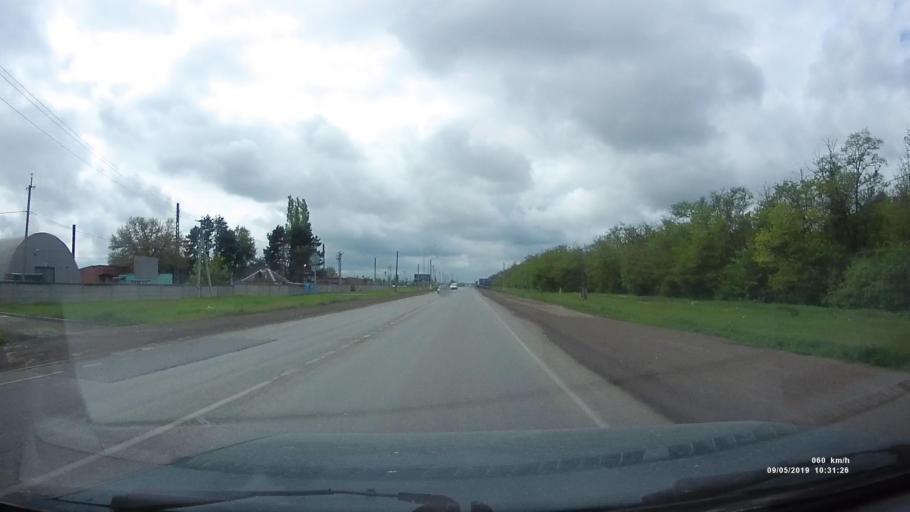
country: RU
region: Rostov
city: Azov
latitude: 47.0819
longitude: 39.4279
